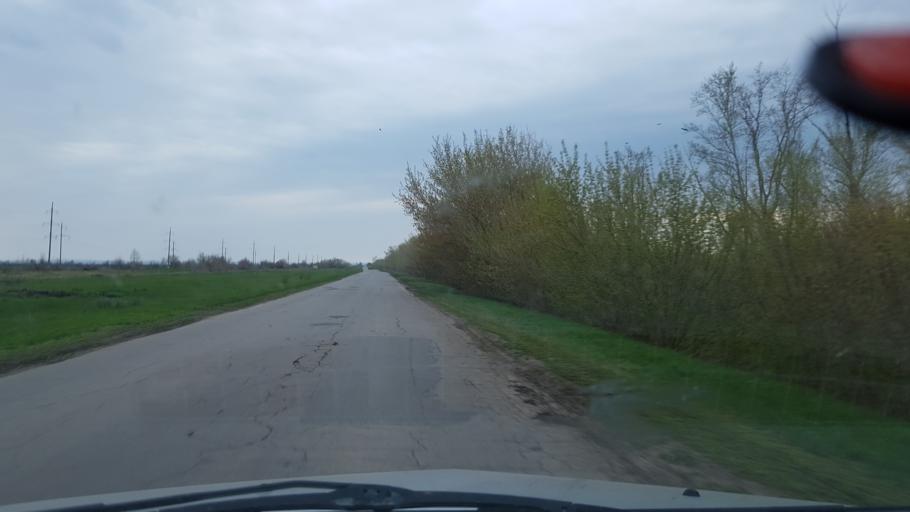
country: RU
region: Samara
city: Podstepki
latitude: 53.6677
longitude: 49.1473
